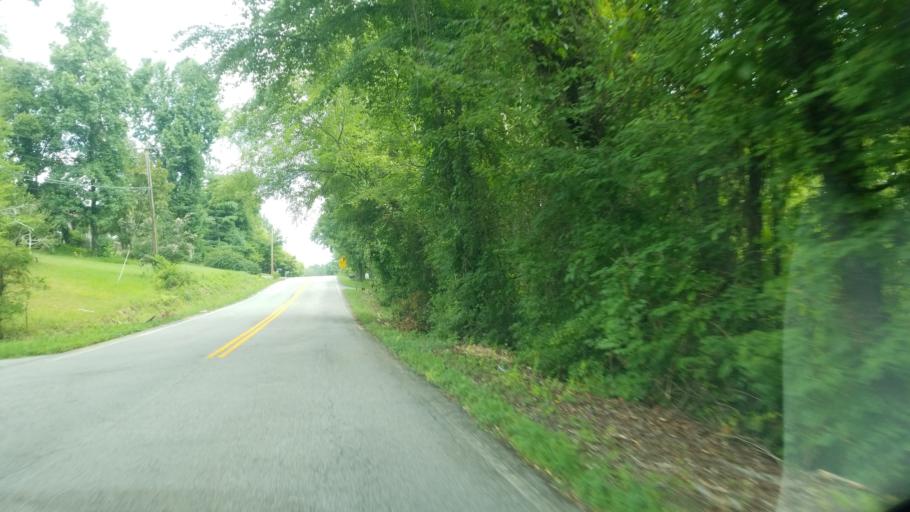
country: US
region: Tennessee
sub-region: Hamilton County
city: Lakesite
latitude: 35.1748
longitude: -85.0915
